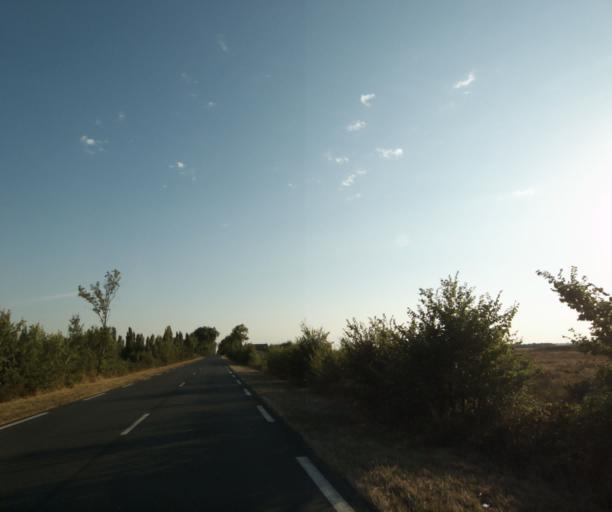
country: FR
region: Poitou-Charentes
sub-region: Departement de la Charente-Maritime
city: Tonnay-Charente
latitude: 45.9630
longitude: -0.9271
